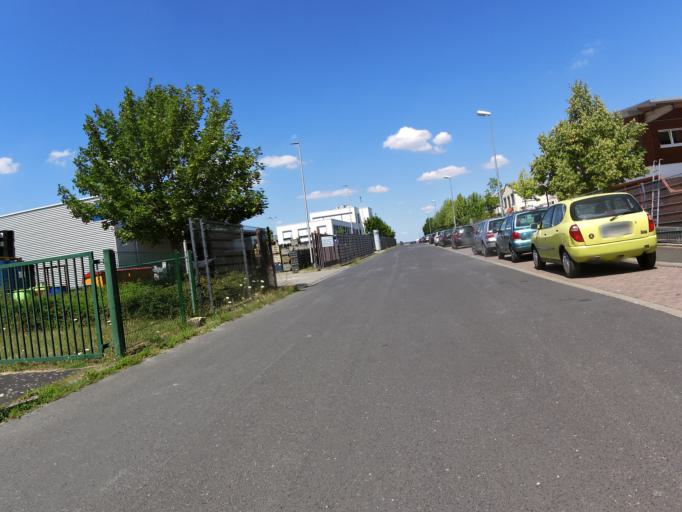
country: DE
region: Bavaria
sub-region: Regierungsbezirk Unterfranken
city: Gadheim
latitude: 49.8310
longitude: 9.9078
